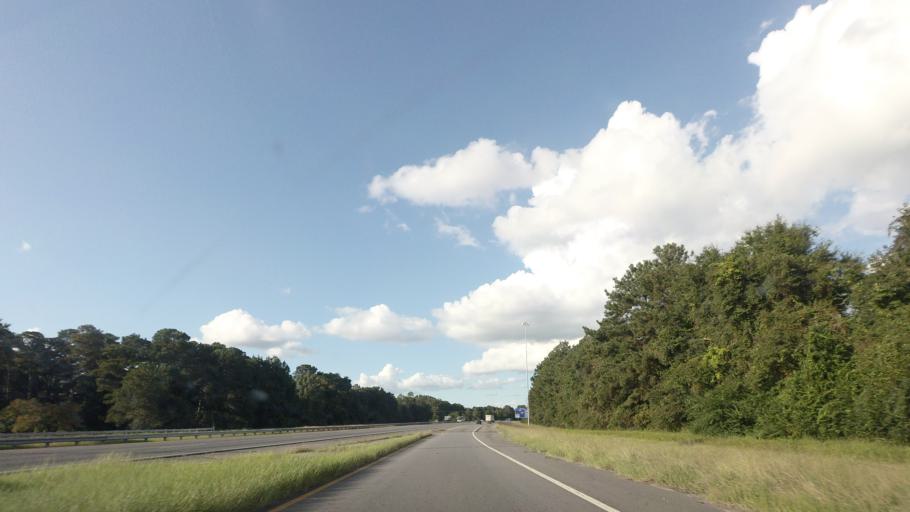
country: US
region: Georgia
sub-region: Houston County
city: Perry
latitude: 32.4496
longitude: -83.7539
